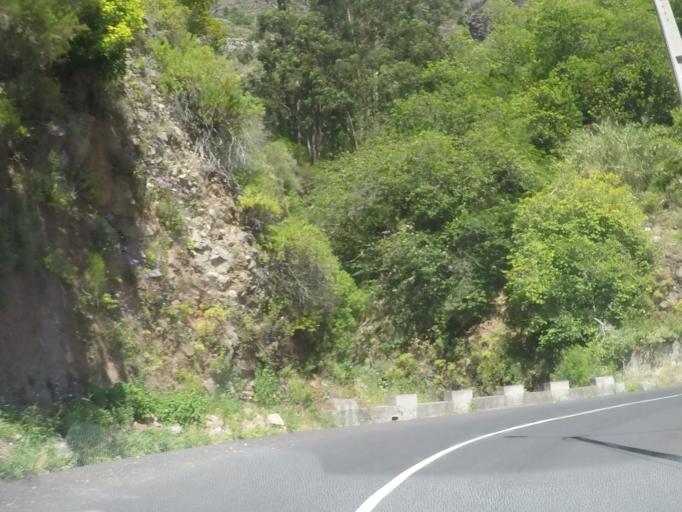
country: PT
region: Madeira
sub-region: Camara de Lobos
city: Curral das Freiras
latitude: 32.7175
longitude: -16.9651
